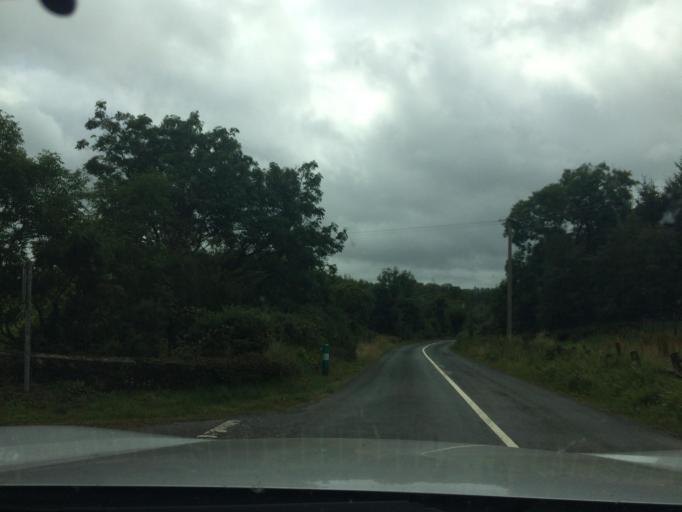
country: IE
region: Munster
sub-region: South Tipperary
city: Cluain Meala
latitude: 52.2219
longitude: -7.7274
